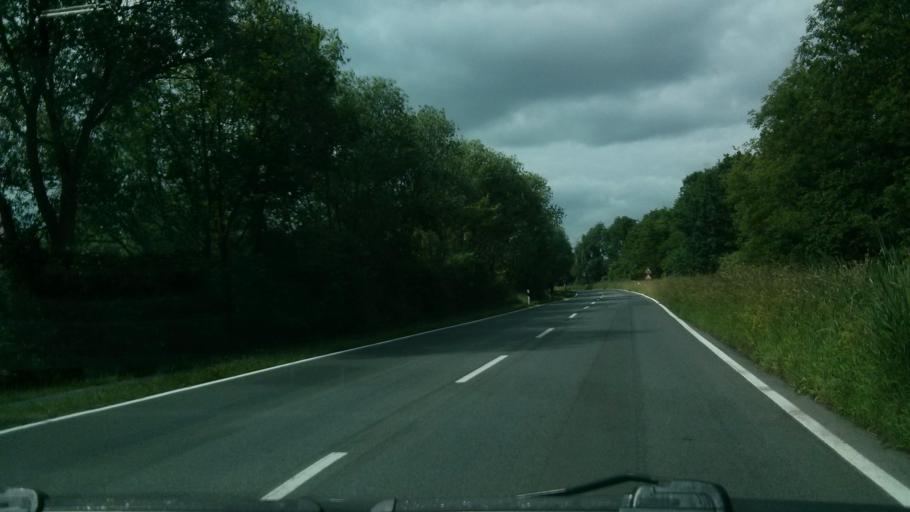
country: DE
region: Lower Saxony
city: Nordenham
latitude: 53.4329
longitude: 8.4761
